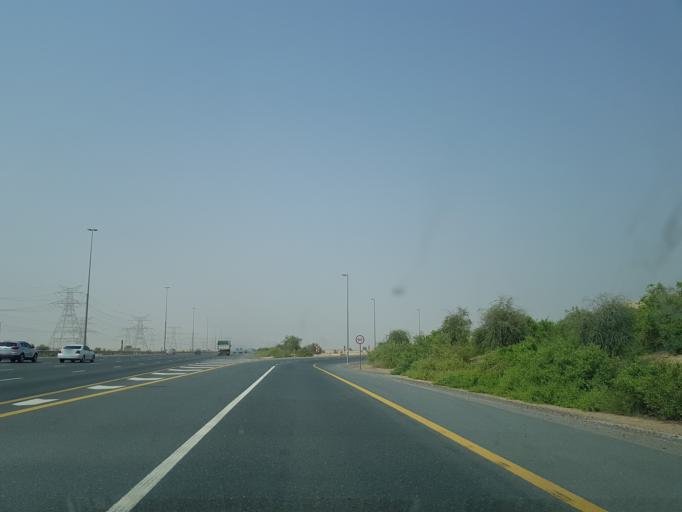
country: AE
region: Dubai
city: Dubai
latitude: 25.0528
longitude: 55.3116
